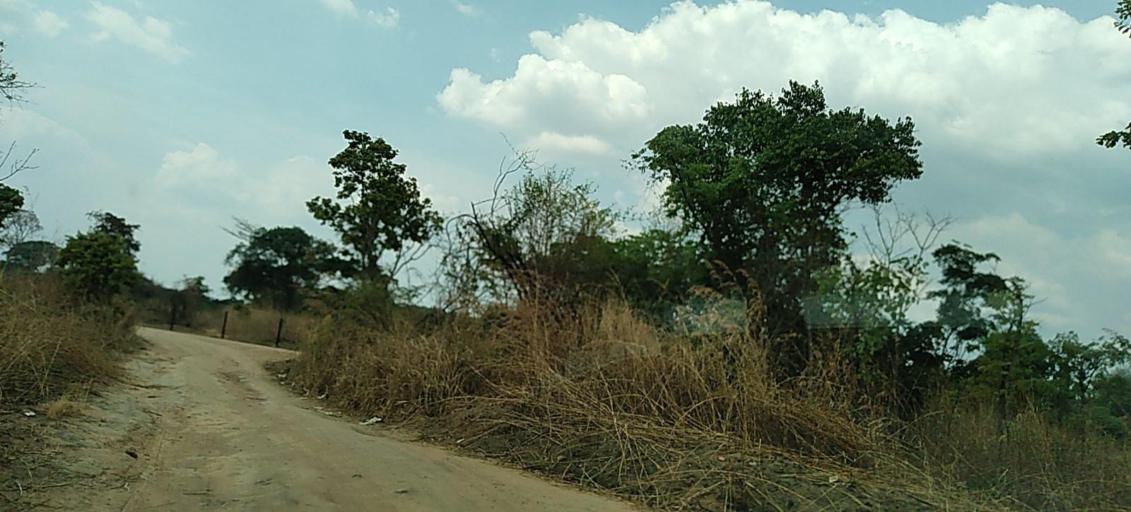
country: ZM
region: Copperbelt
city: Chililabombwe
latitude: -12.3195
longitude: 27.7492
